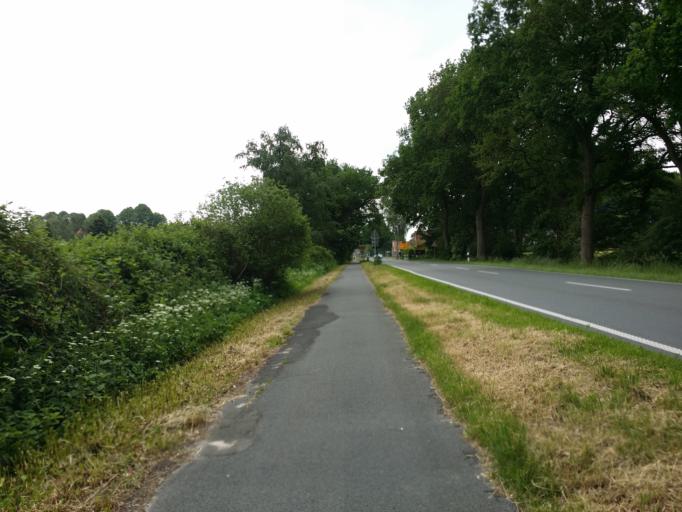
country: DE
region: Lower Saxony
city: Wittmund
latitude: 53.5319
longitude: 7.7818
